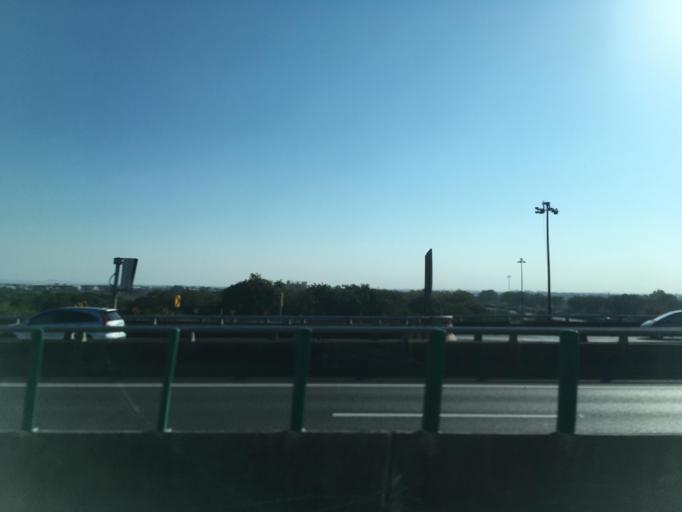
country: TW
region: Taiwan
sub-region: Chiayi
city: Taibao
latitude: 23.4244
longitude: 120.3577
